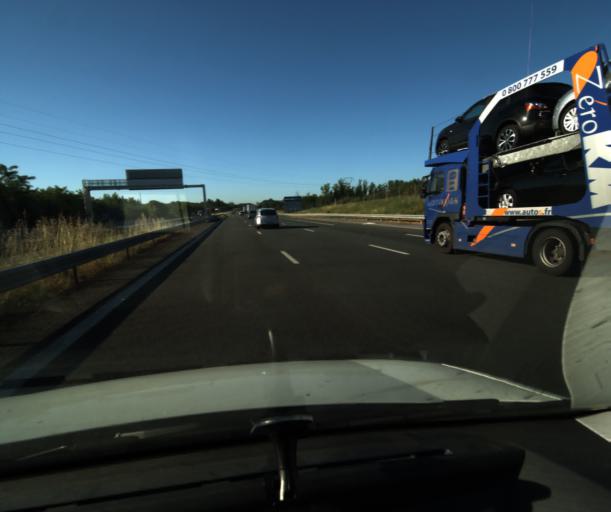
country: FR
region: Midi-Pyrenees
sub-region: Departement du Tarn-et-Garonne
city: Campsas
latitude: 43.8967
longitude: 1.3165
